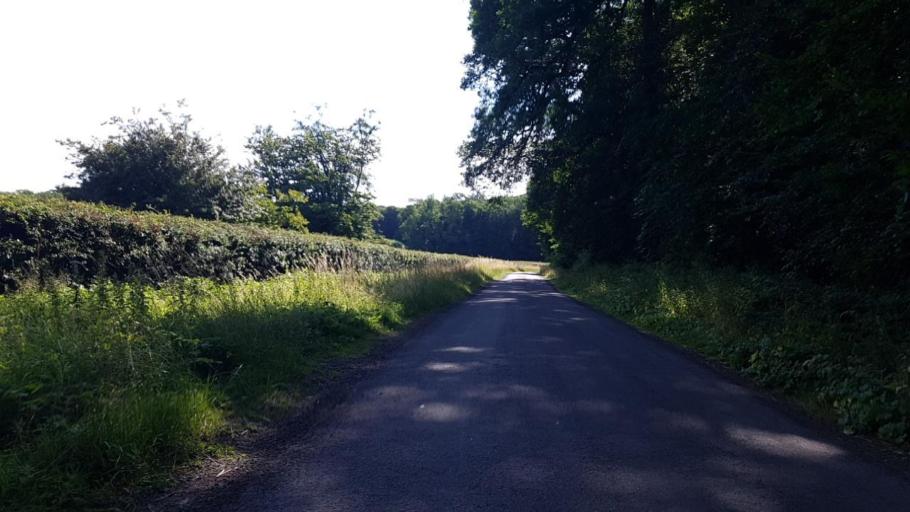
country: FR
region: Picardie
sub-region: Departement de l'Oise
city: Pontpoint
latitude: 49.2910
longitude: 2.6434
